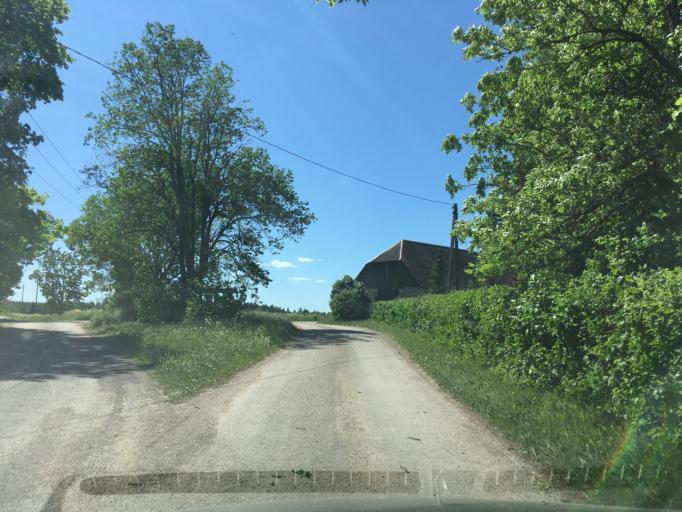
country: EE
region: Harju
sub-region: Rae vald
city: Vaida
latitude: 59.1579
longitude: 25.1262
